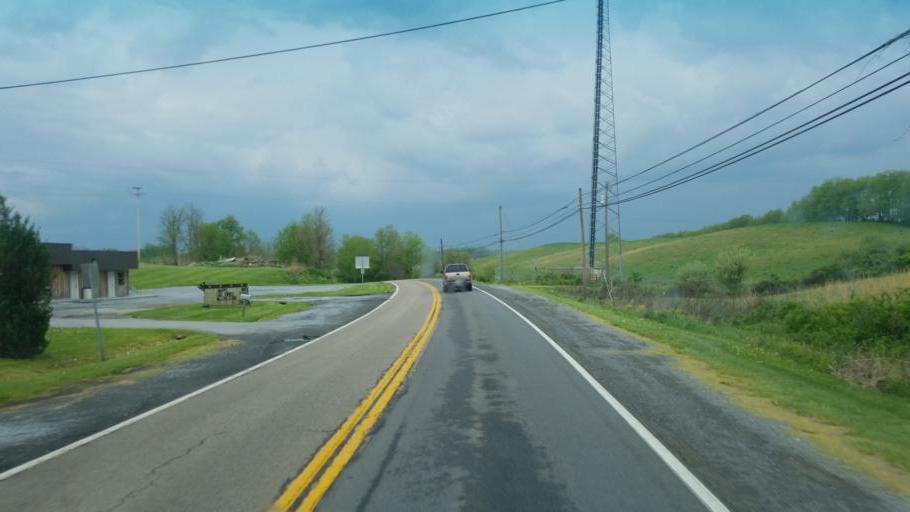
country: US
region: Virginia
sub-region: Smyth County
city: Chilhowie
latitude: 36.7887
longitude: -81.7193
